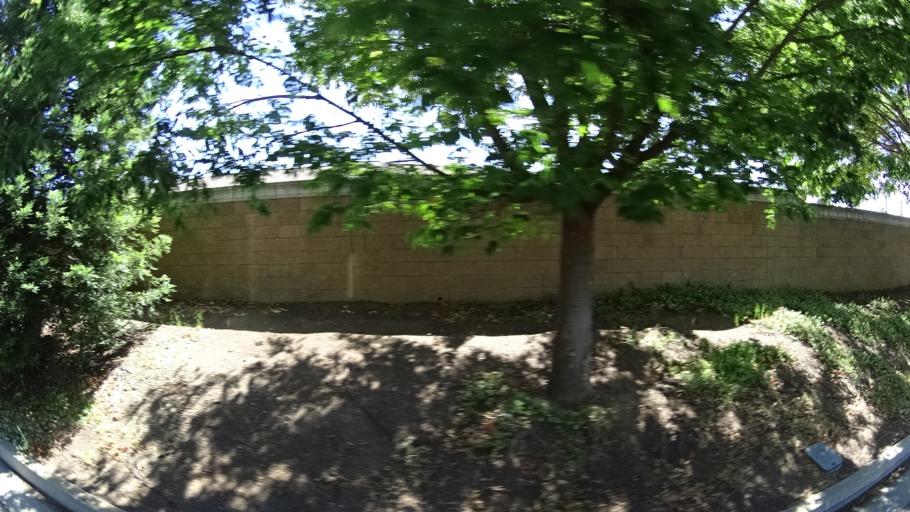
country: US
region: California
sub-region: Sacramento County
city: Parkway
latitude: 38.5093
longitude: -121.5057
